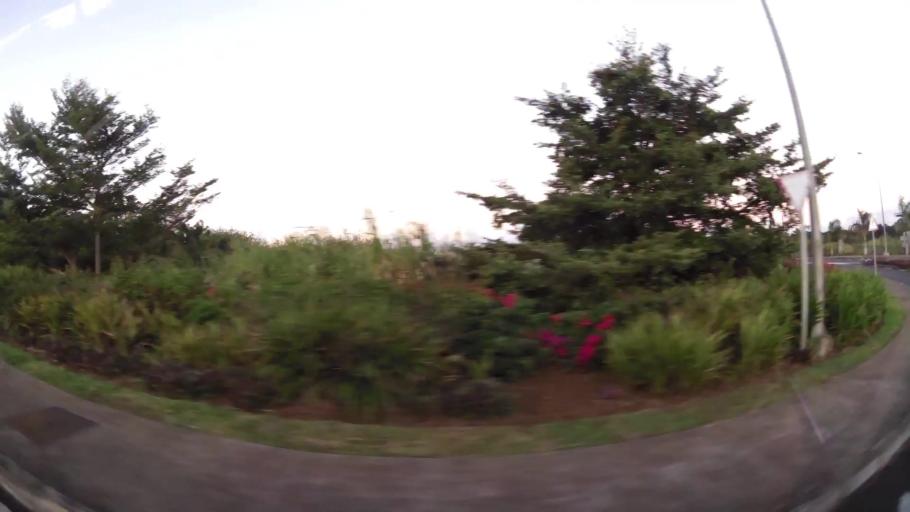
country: MU
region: Moka
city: Moka
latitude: -20.2268
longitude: 57.4922
